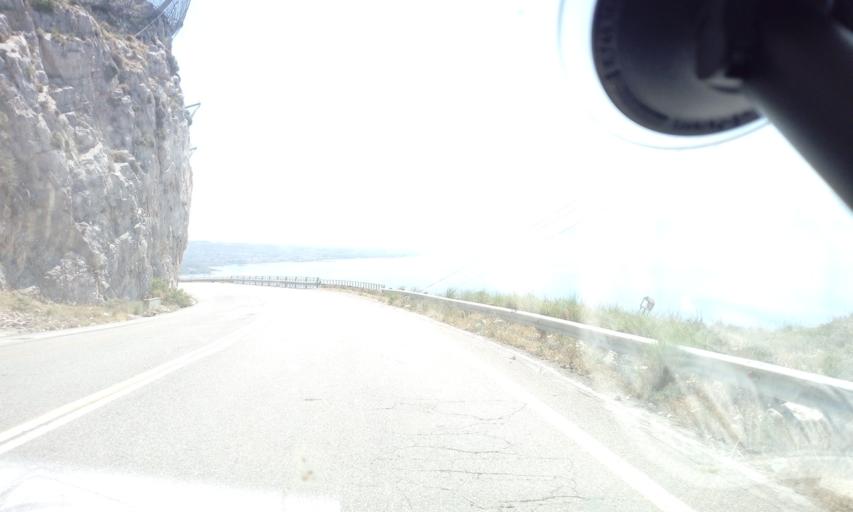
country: GR
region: West Greece
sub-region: Nomos Aitolias kai Akarnanias
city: Antirrio
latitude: 38.3475
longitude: 21.6835
